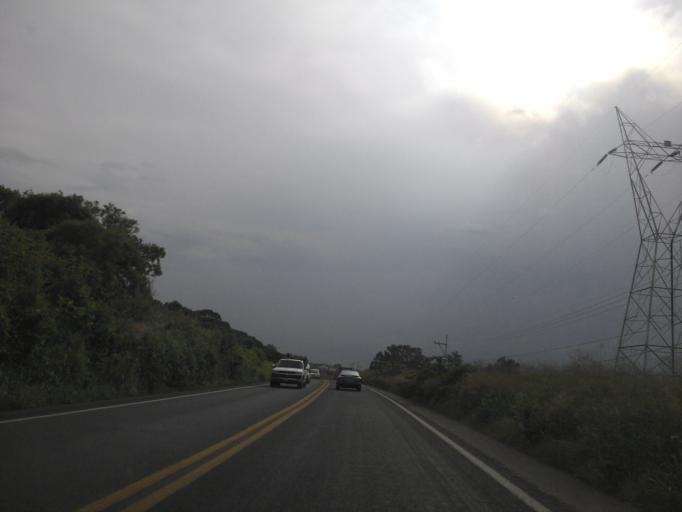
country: MX
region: Jalisco
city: Acatic
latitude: 20.7116
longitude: -102.9459
